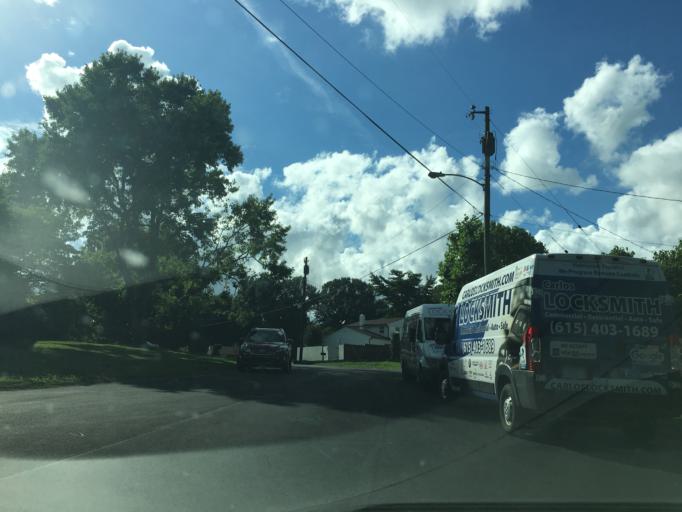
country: US
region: Tennessee
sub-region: Davidson County
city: Oak Hill
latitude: 36.0907
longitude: -86.7242
